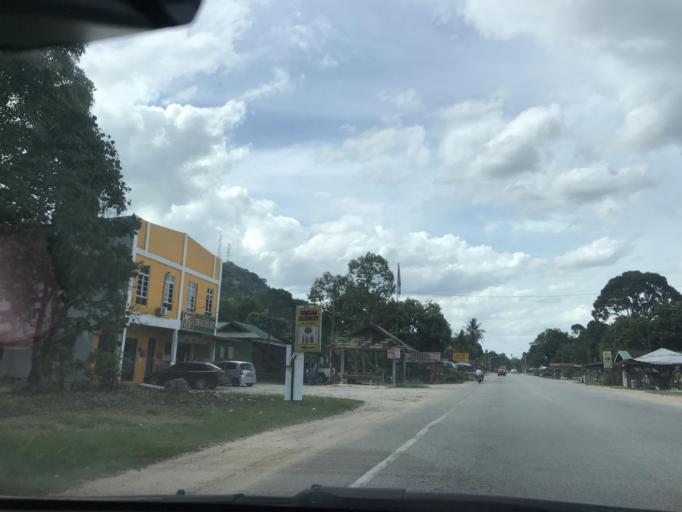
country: MY
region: Kelantan
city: Kampong Pangkal Kalong
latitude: 5.8818
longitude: 102.1766
